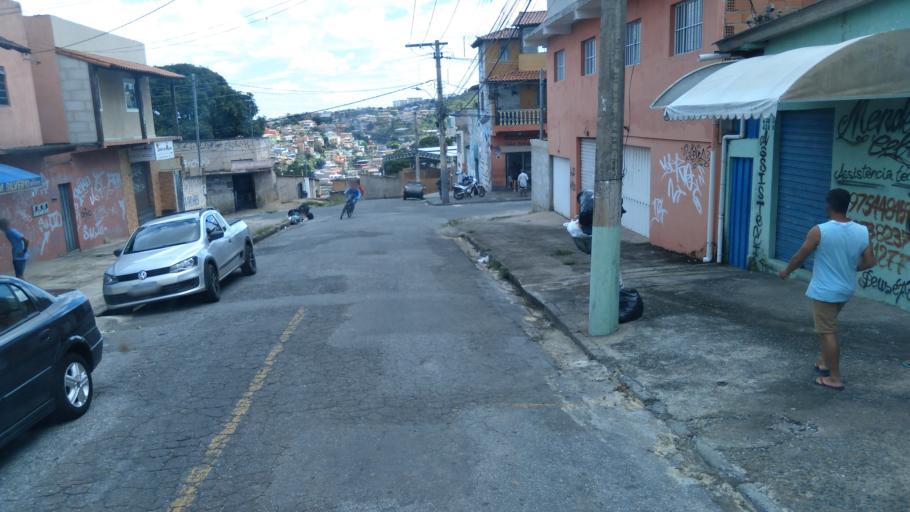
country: BR
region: Minas Gerais
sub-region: Belo Horizonte
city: Belo Horizonte
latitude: -19.8532
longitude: -43.9020
